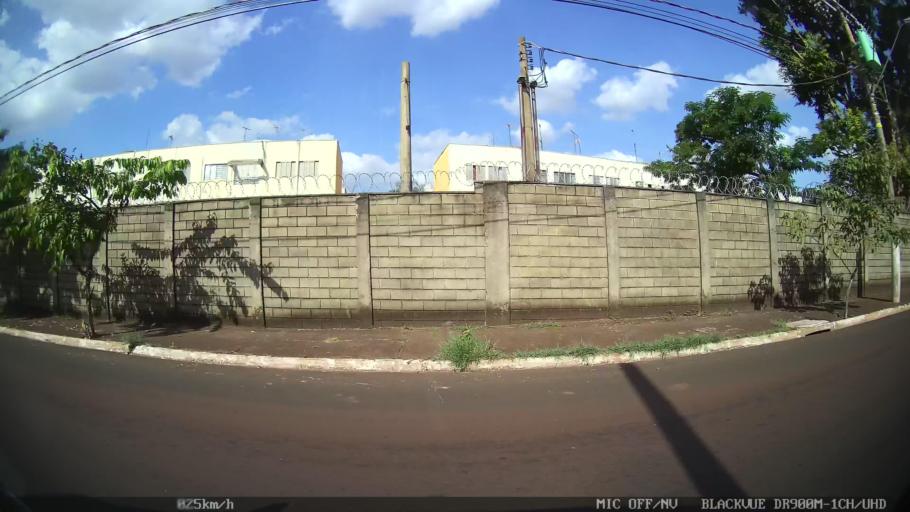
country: BR
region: Sao Paulo
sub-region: Ribeirao Preto
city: Ribeirao Preto
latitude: -21.1906
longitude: -47.8265
